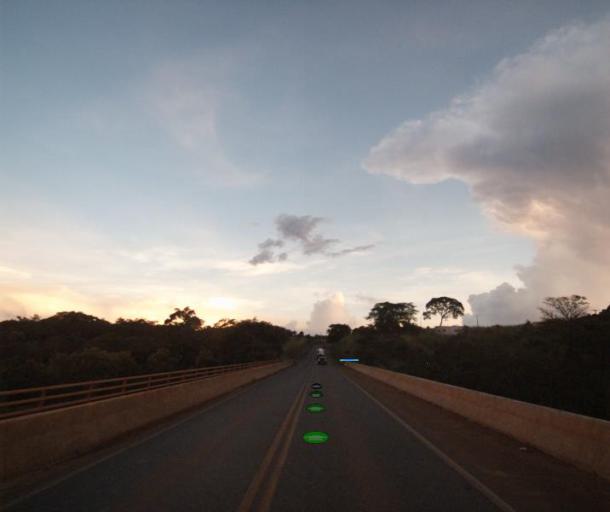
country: BR
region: Goias
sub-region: Uruacu
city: Uruacu
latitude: -14.5038
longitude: -49.1492
